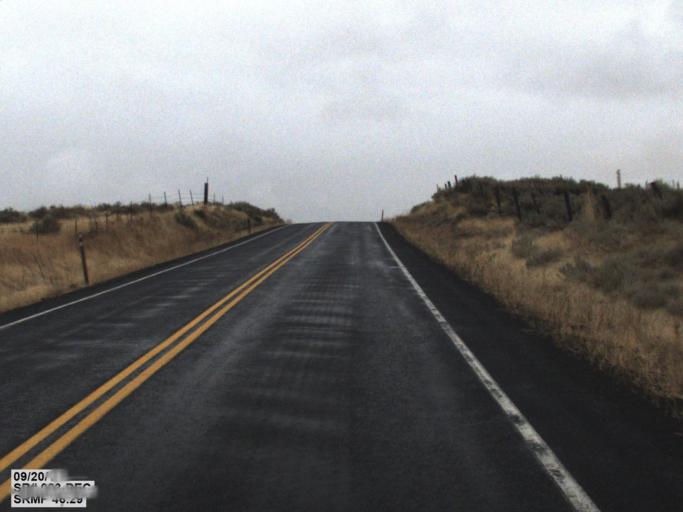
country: US
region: Washington
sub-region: Lincoln County
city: Davenport
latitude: 47.3339
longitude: -117.9976
